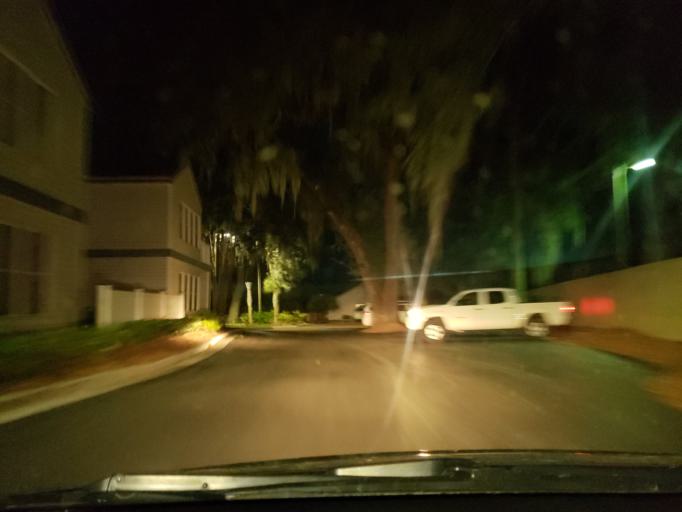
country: US
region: Georgia
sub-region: Chatham County
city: Montgomery
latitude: 31.9780
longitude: -81.1282
